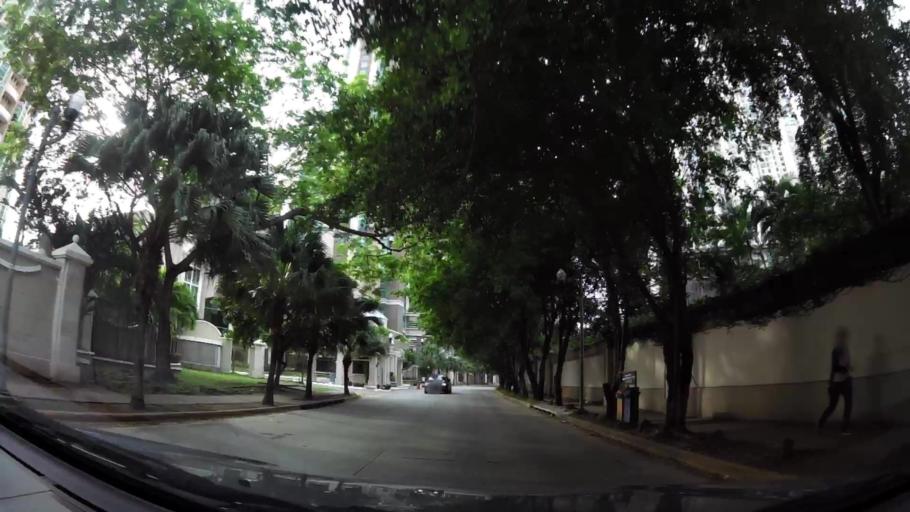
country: PA
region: Panama
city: Panama
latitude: 8.9783
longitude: -79.5078
